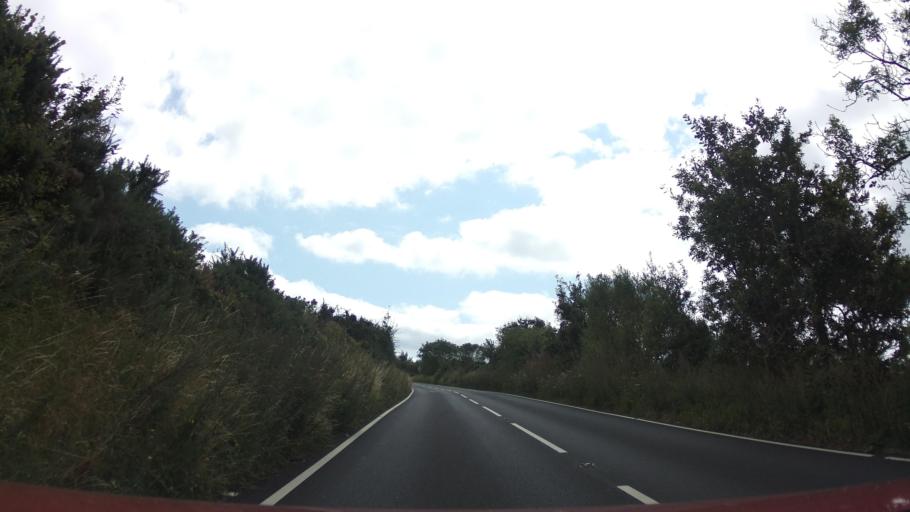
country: GB
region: England
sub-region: Devon
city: Bishopsteignton
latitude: 50.5829
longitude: -3.5323
